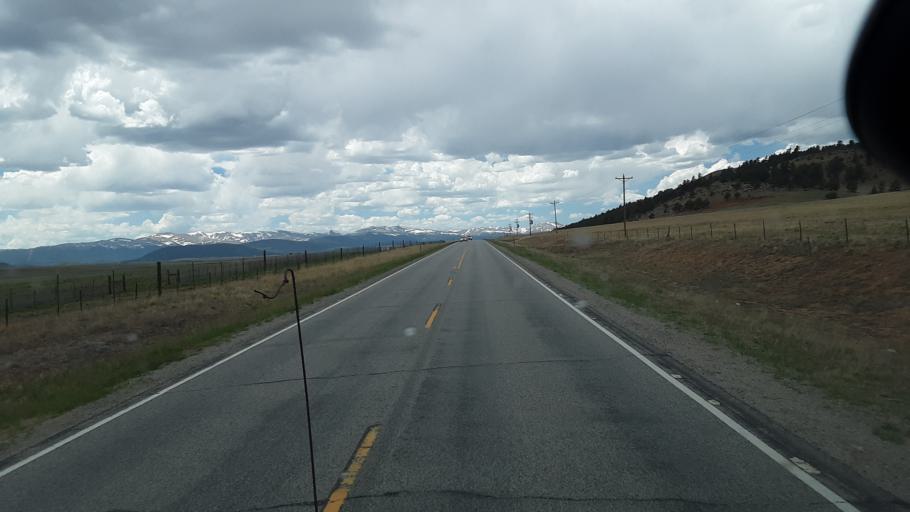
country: US
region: Colorado
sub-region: Park County
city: Fairplay
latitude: 39.0451
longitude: -105.8363
